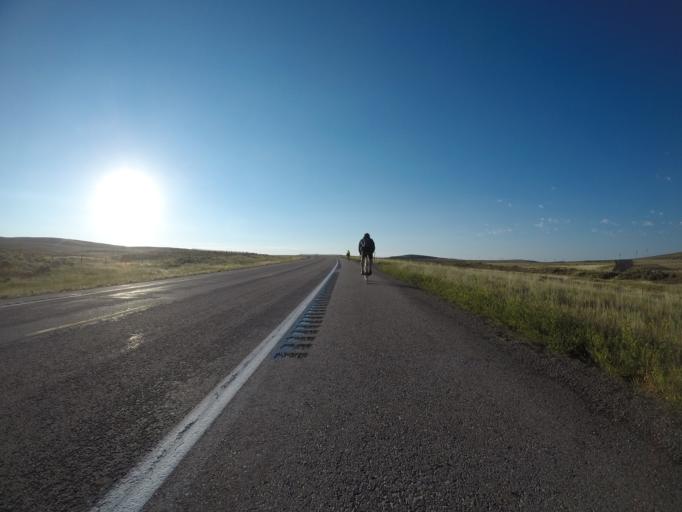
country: US
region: Wyoming
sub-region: Lincoln County
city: Kemmerer
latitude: 41.8688
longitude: -110.4707
